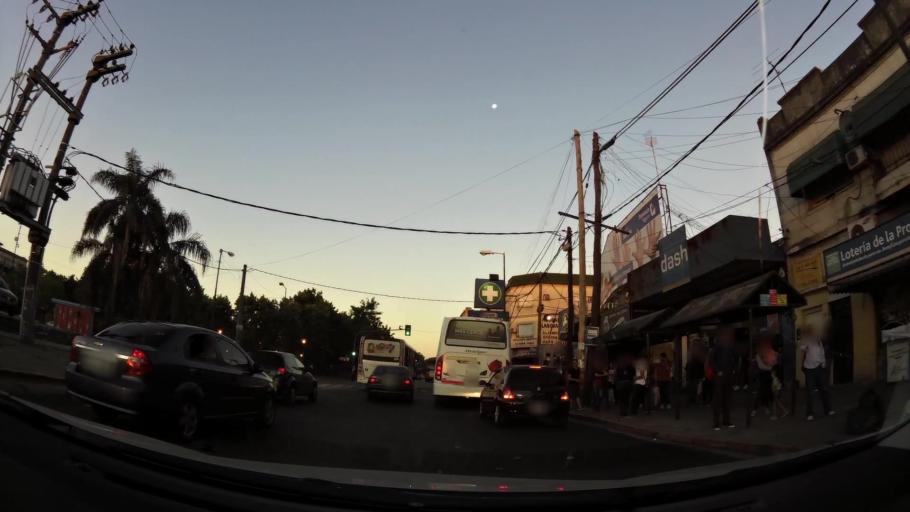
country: AR
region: Buenos Aires
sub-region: Partido de Tigre
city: Tigre
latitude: -34.4351
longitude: -58.5664
